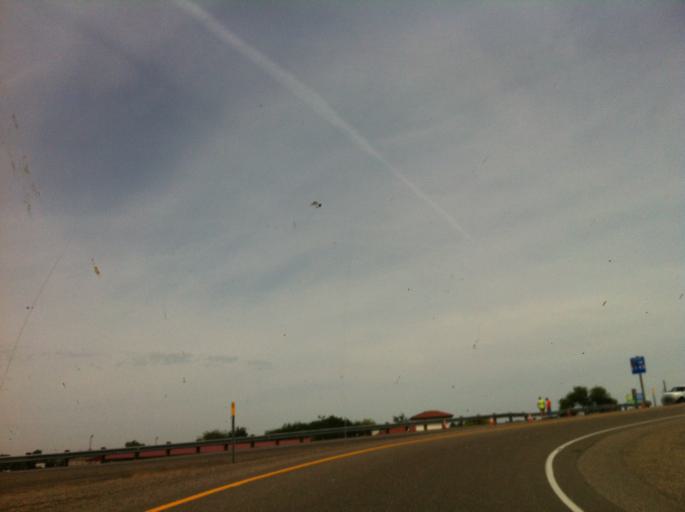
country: US
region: Oregon
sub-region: Malheur County
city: Ontario
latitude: 44.0268
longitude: -116.9500
